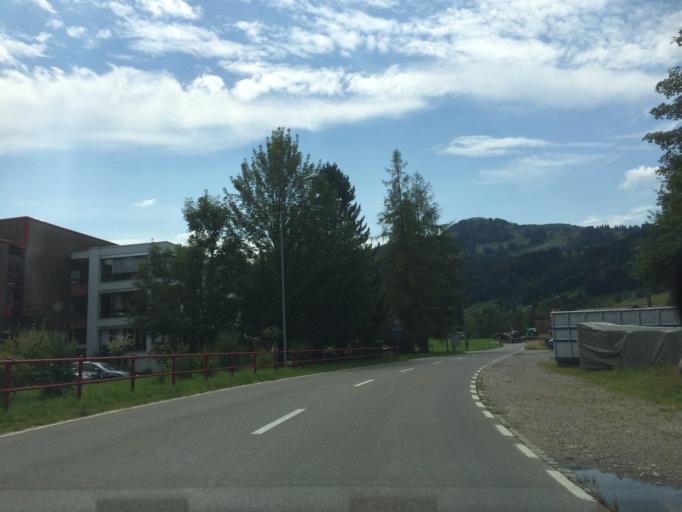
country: CH
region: Appenzell Ausserrhoden
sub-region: Bezirk Hinterland
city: Urnasch
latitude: 47.3035
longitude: 9.2744
